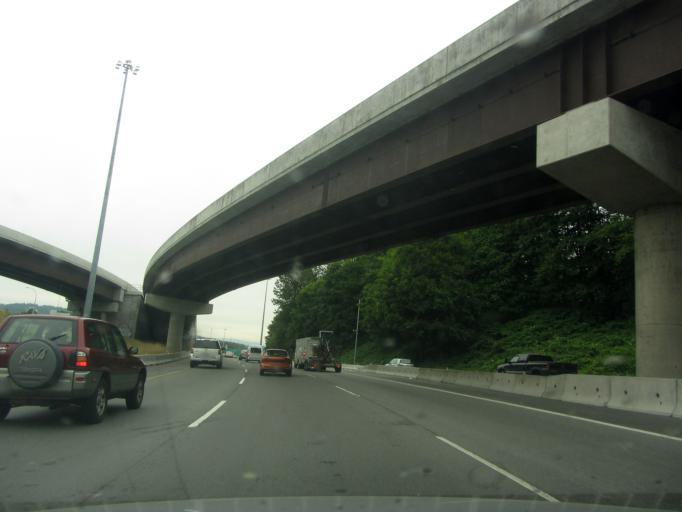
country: CA
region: British Columbia
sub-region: Fraser Valley Regional District
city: North Vancouver
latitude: 49.2693
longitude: -123.0352
